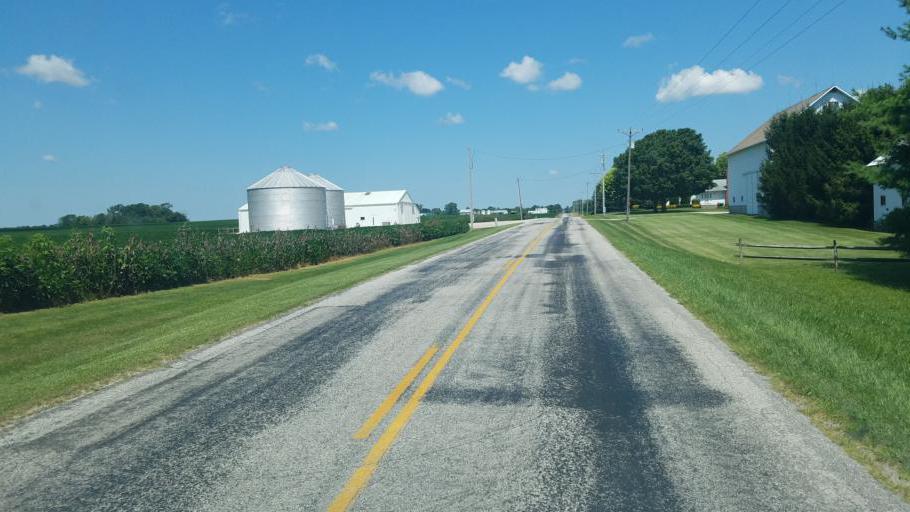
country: US
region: Ohio
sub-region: Marion County
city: Prospect
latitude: 40.5083
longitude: -83.2032
